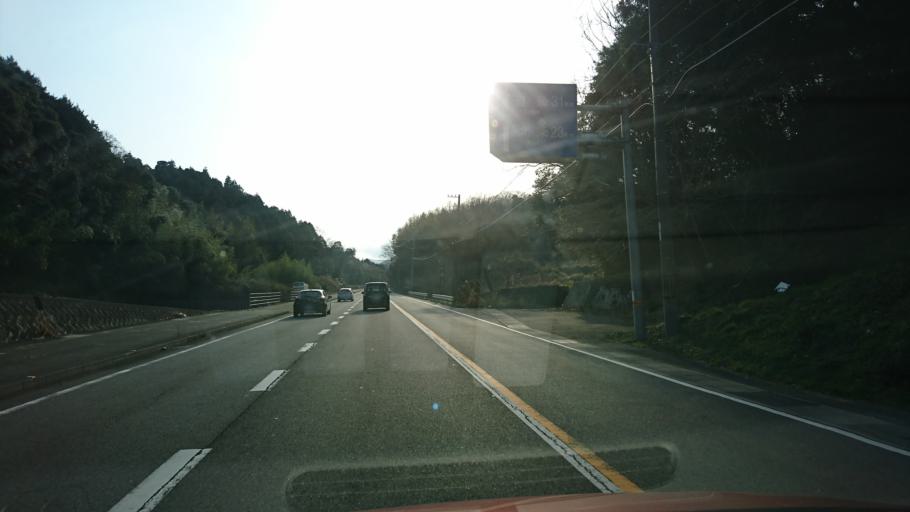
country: JP
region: Ehime
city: Hojo
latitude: 34.0004
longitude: 132.9366
